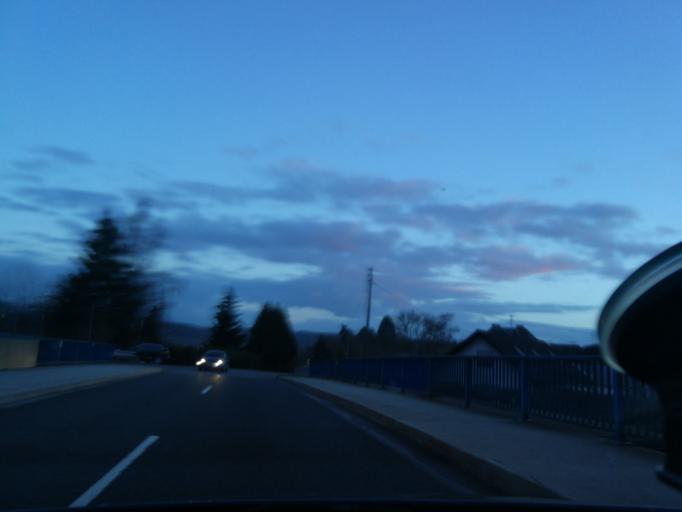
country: DE
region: Rheinland-Pfalz
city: Kenn
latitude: 49.8258
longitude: 6.7041
